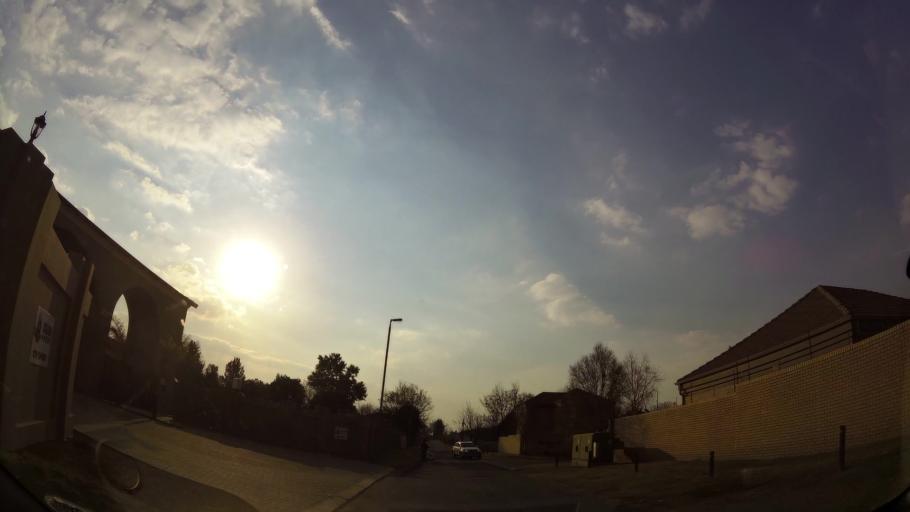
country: ZA
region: Gauteng
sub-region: Ekurhuleni Metropolitan Municipality
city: Benoni
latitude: -26.1262
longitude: 28.2913
